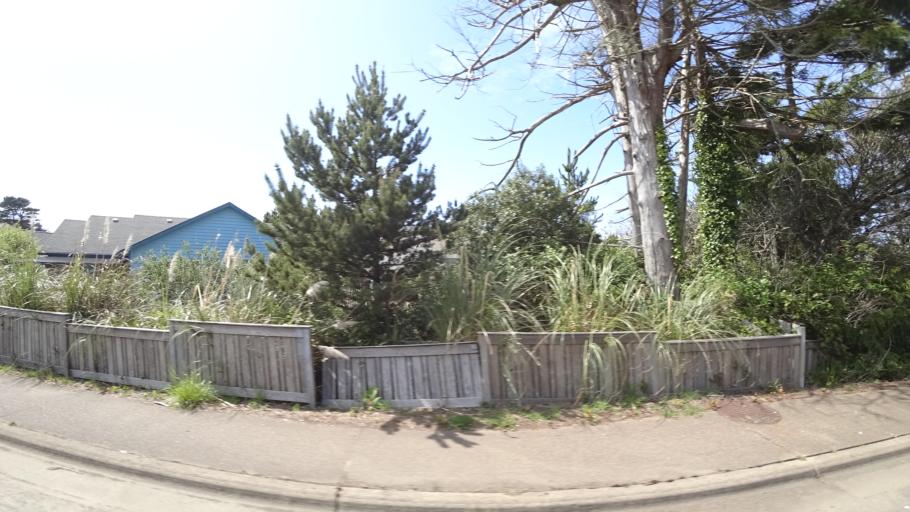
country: US
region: Oregon
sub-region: Lincoln County
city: Lincoln Beach
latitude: 44.8510
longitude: -124.0438
